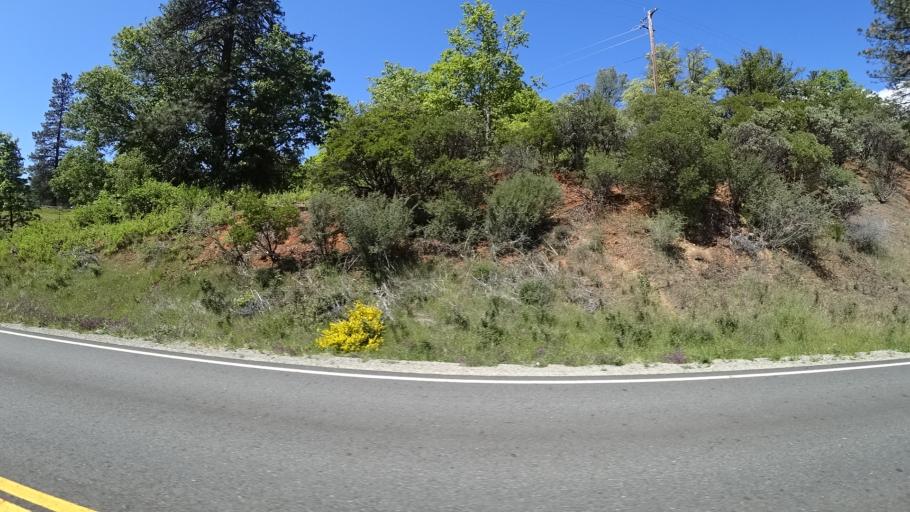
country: US
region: California
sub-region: Trinity County
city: Weaverville
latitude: 40.7292
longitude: -123.0373
